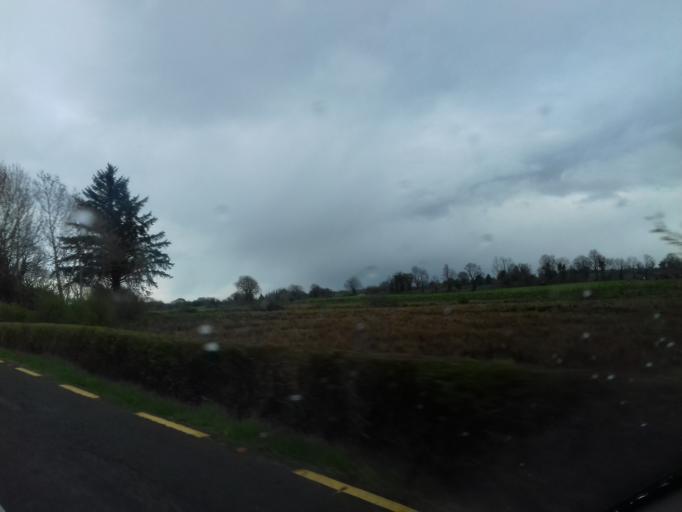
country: IE
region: Ulster
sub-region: An Cabhan
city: Ballyconnell
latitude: 54.1529
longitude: -7.7153
